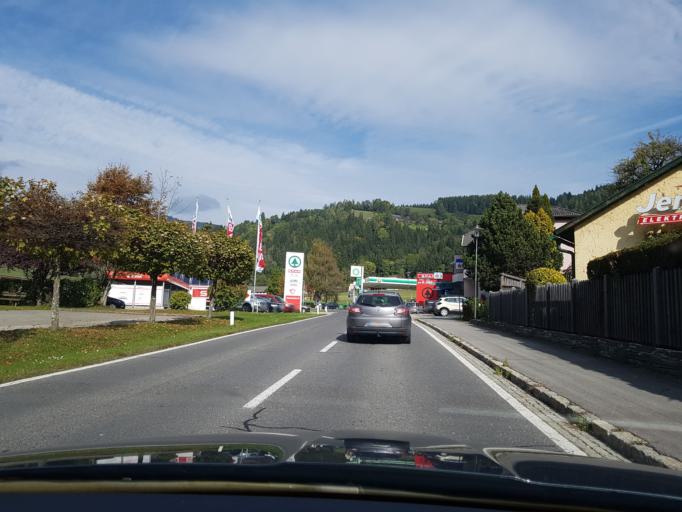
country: AT
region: Carinthia
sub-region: Politischer Bezirk Feldkirchen
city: Himmelberg
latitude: 46.7509
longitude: 14.0345
